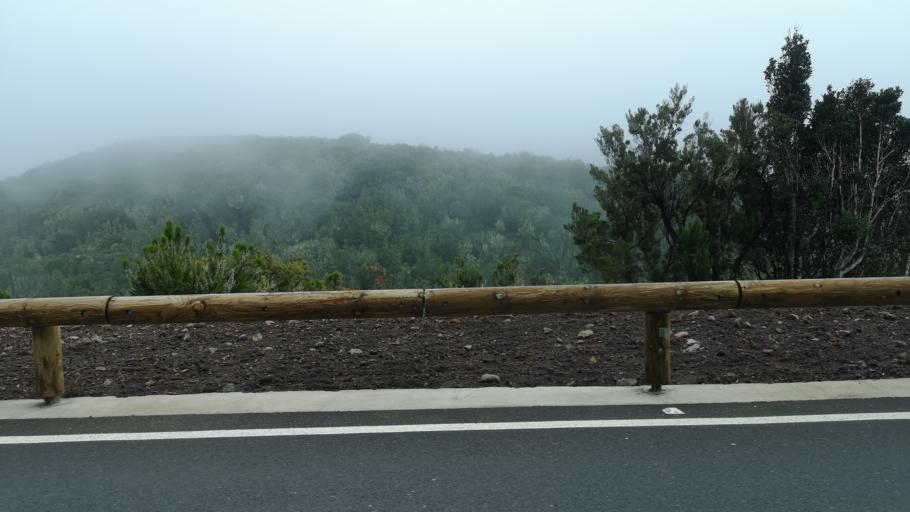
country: ES
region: Canary Islands
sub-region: Provincia de Santa Cruz de Tenerife
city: Vallehermosa
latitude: 28.1484
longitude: -17.3087
